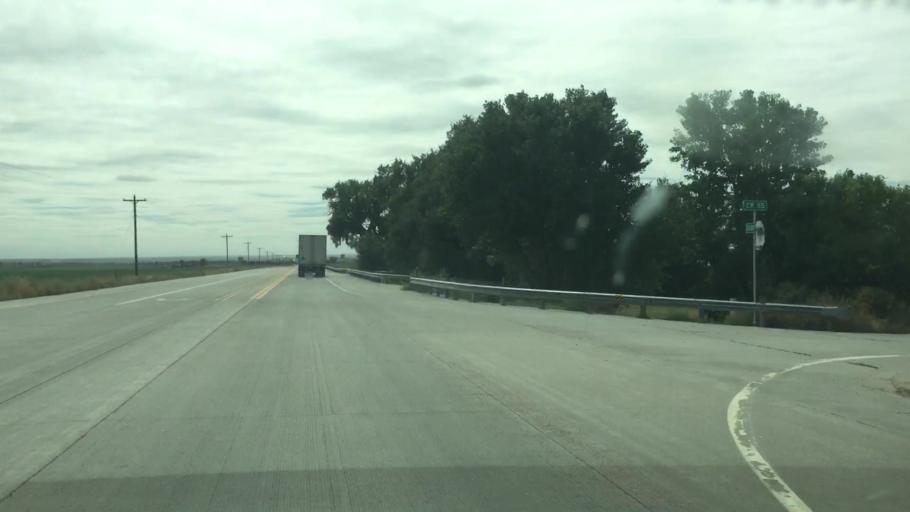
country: US
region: Colorado
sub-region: Prowers County
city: Lamar
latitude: 38.2016
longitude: -102.7242
